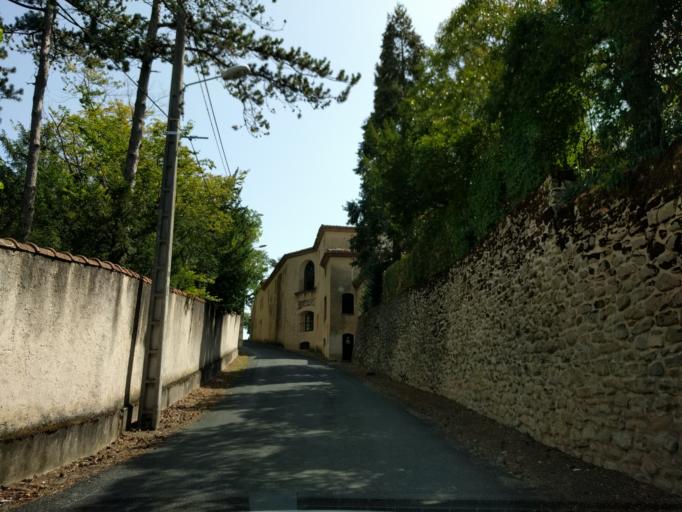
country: FR
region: Midi-Pyrenees
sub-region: Departement du Tarn
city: Castres
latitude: 43.5992
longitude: 2.2487
